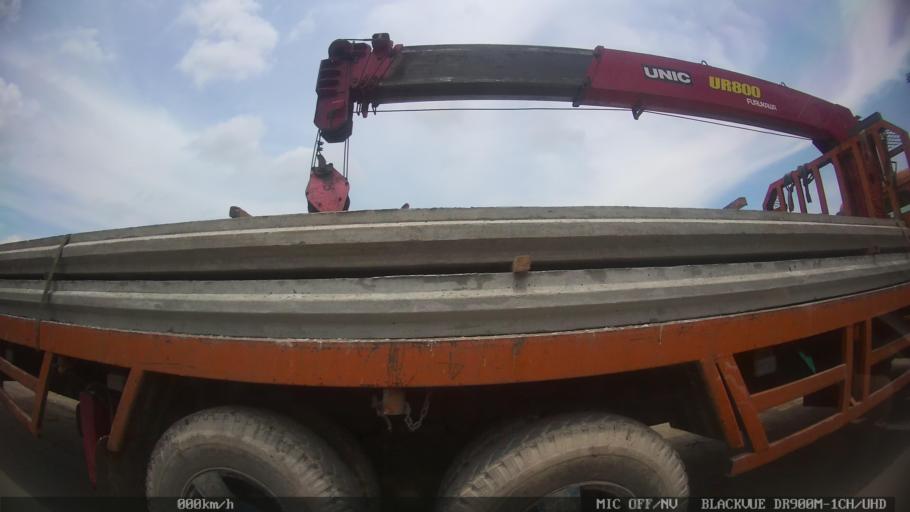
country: ID
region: North Sumatra
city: Labuhan Deli
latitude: 3.6943
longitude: 98.6937
